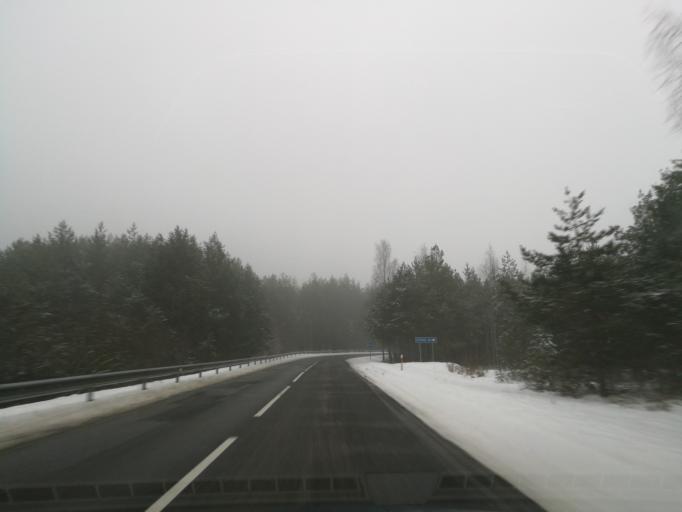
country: LT
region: Vilnius County
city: Ukmerge
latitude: 55.3329
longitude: 24.8891
